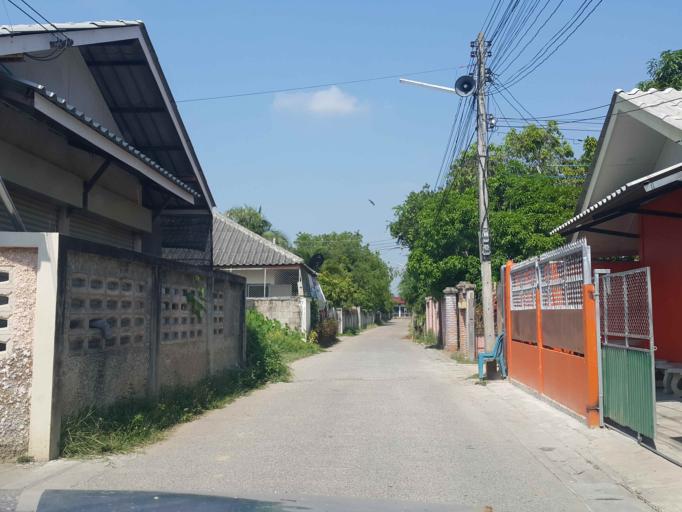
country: TH
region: Chiang Mai
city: Saraphi
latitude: 18.7752
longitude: 99.0563
